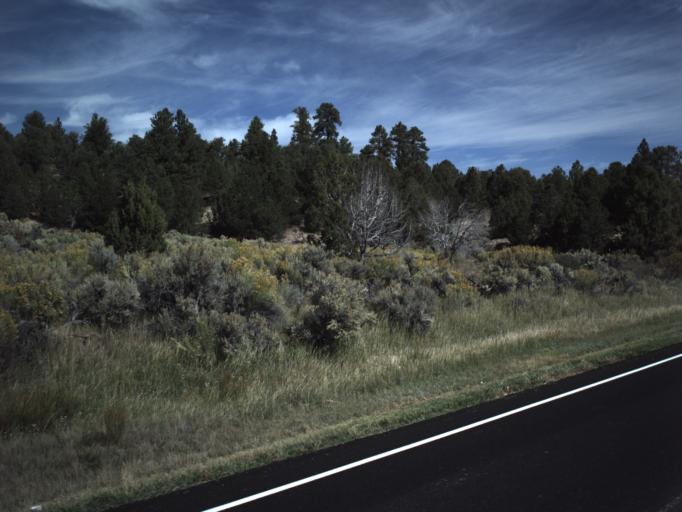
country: US
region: Utah
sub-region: Garfield County
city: Panguitch
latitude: 37.6957
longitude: -111.7943
